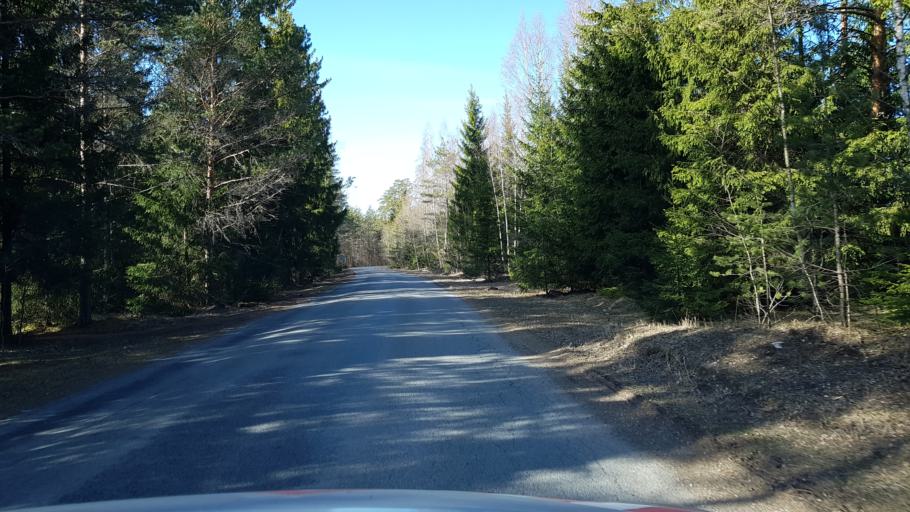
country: EE
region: Harju
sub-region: Nissi vald
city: Riisipere
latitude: 59.0819
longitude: 24.3555
